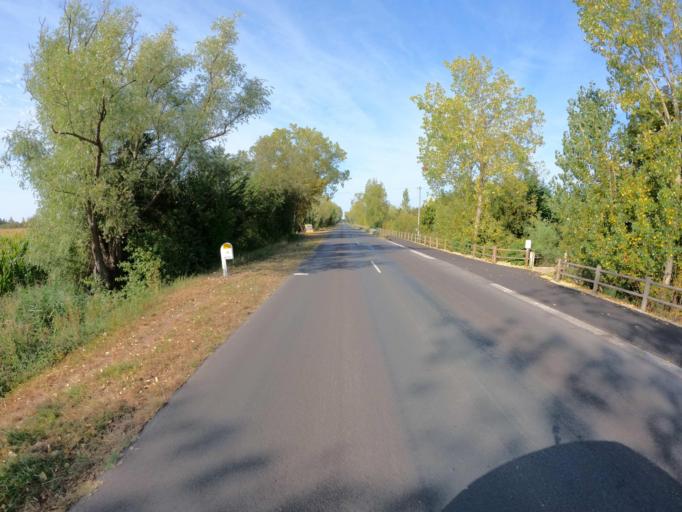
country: FR
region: Pays de la Loire
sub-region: Departement de la Vendee
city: Saint-Jean-de-Monts
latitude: 46.8000
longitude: -2.0383
